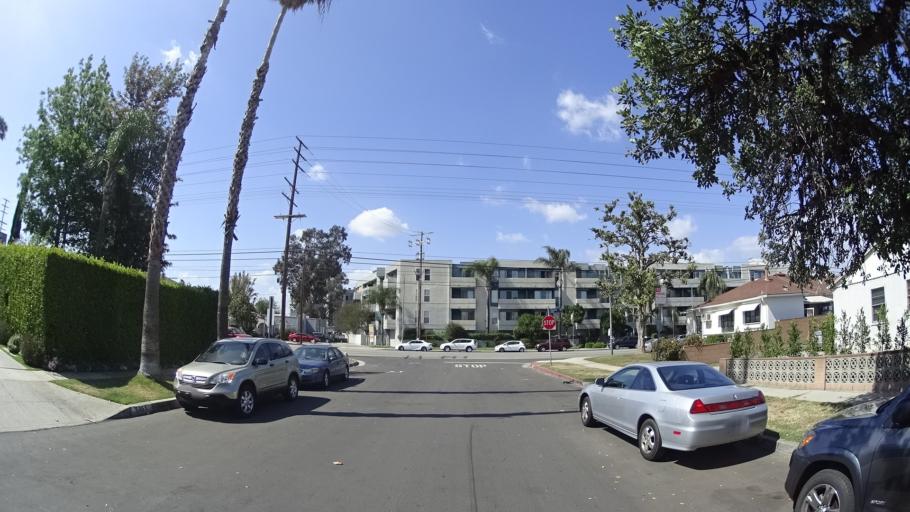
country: US
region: California
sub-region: Los Angeles County
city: North Hollywood
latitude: 34.1790
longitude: -118.3866
